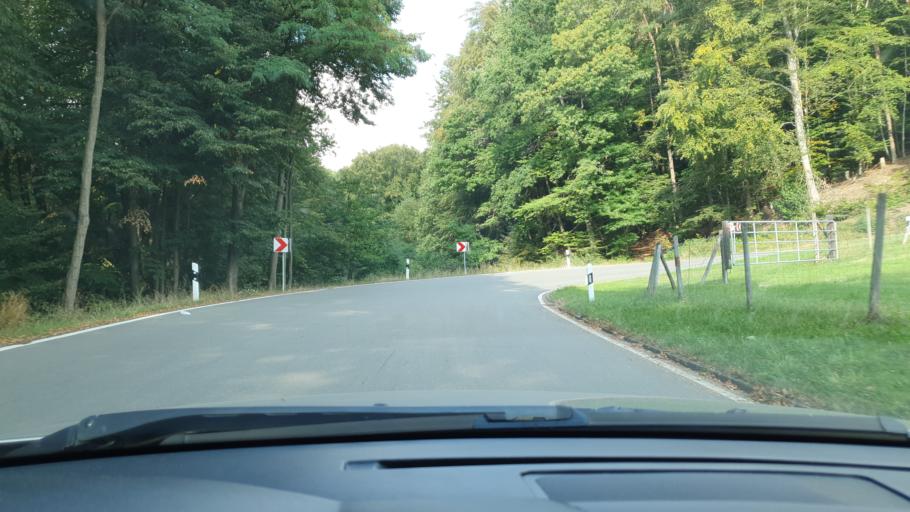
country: DE
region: Rheinland-Pfalz
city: Oberarnbach
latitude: 49.3909
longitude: 7.5870
